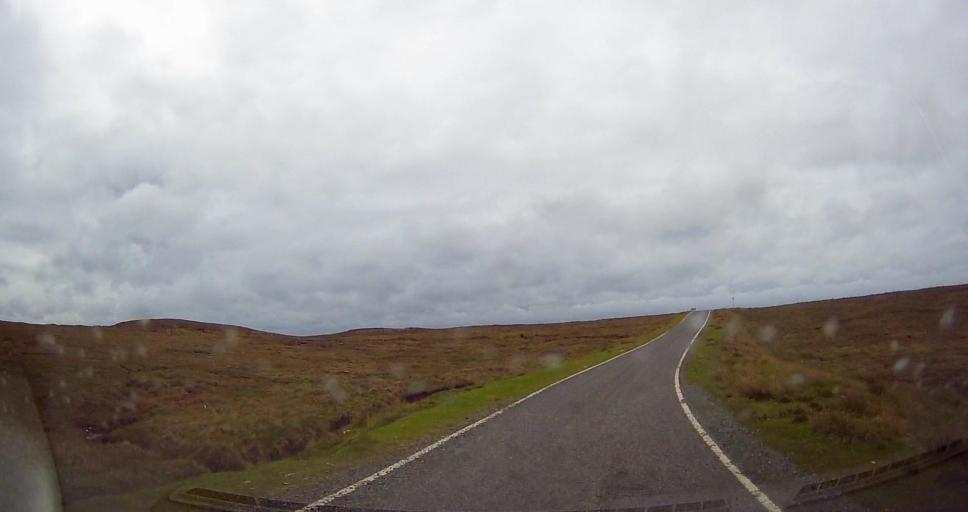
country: GB
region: Scotland
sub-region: Shetland Islands
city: Lerwick
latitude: 60.4924
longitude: -1.5711
